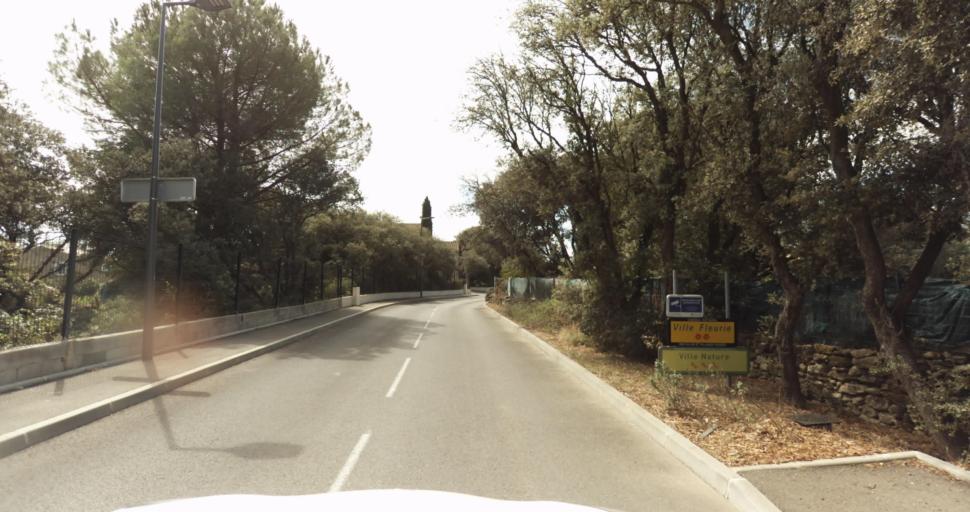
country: FR
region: Provence-Alpes-Cote d'Azur
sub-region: Departement des Bouches-du-Rhone
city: Miramas
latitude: 43.5799
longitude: 5.0260
